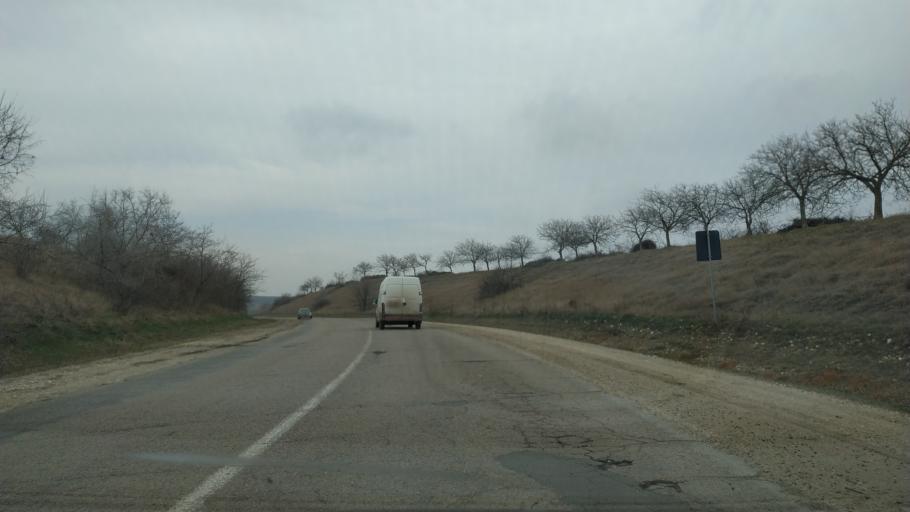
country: MD
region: Cahul
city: Cahul
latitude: 45.9600
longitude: 28.3885
